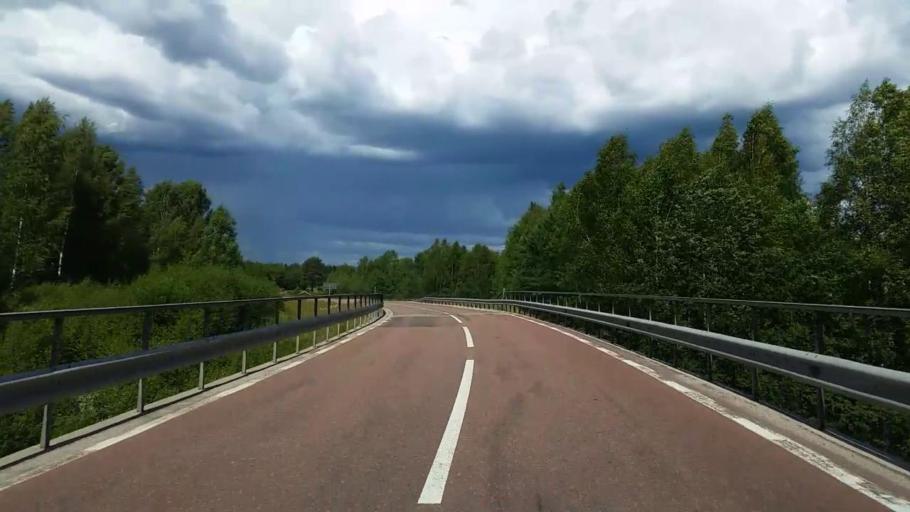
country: SE
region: Gaevleborg
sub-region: Ovanakers Kommun
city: Edsbyn
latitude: 61.3357
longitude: 15.5426
